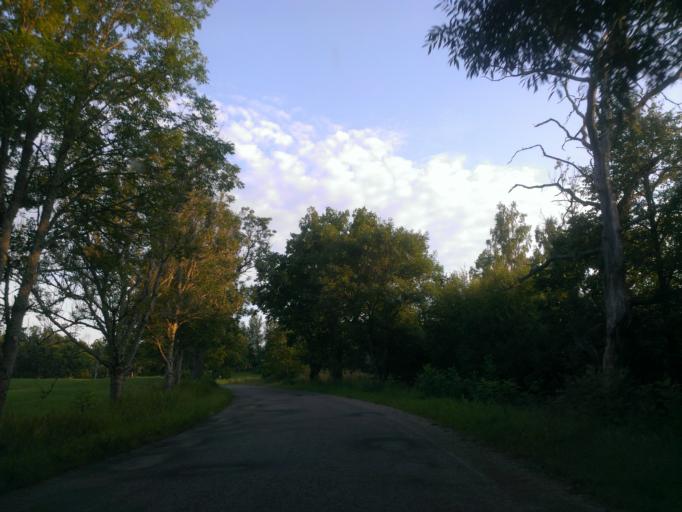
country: LV
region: Amatas Novads
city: Drabesi
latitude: 57.2483
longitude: 25.2786
